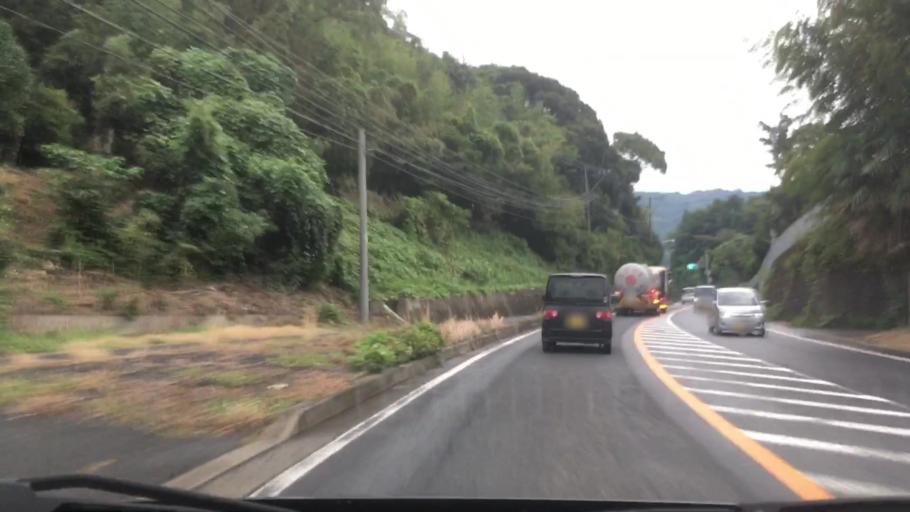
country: JP
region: Nagasaki
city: Sasebo
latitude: 33.1043
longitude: 129.7731
